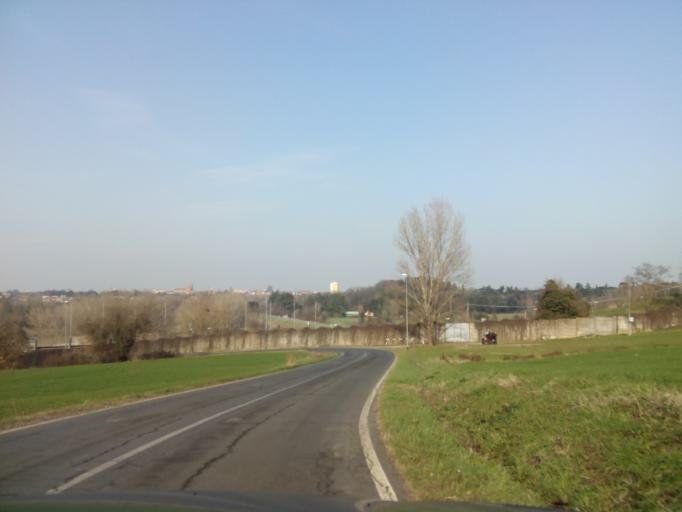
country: IT
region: Emilia-Romagna
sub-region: Provincia di Bologna
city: Imola
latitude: 44.3352
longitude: 11.7012
